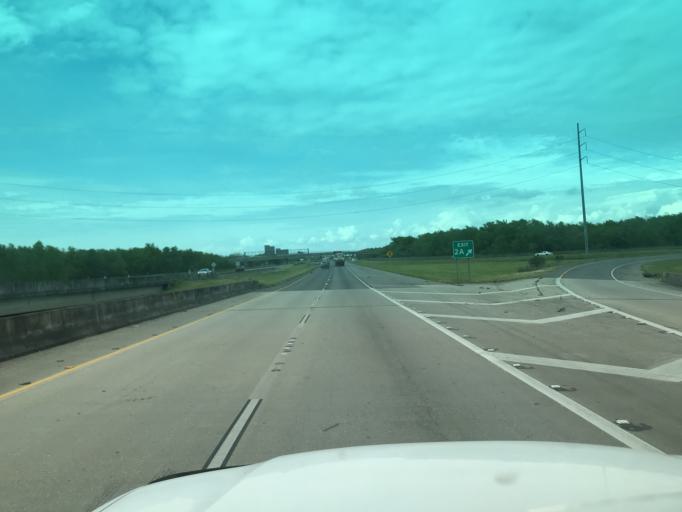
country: US
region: Louisiana
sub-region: Saint Bernard Parish
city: Chalmette
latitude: 30.0292
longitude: -89.9393
